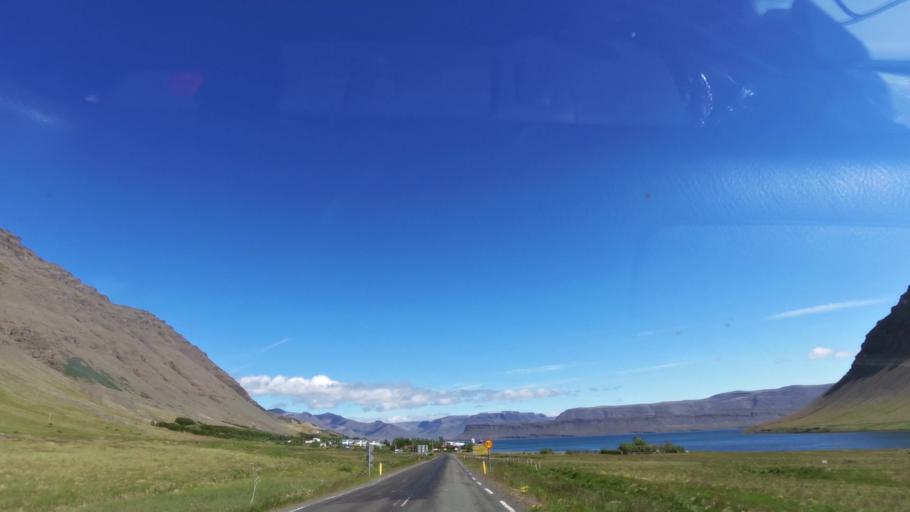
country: IS
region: Westfjords
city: Isafjoerdur
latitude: 65.6749
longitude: -23.6169
